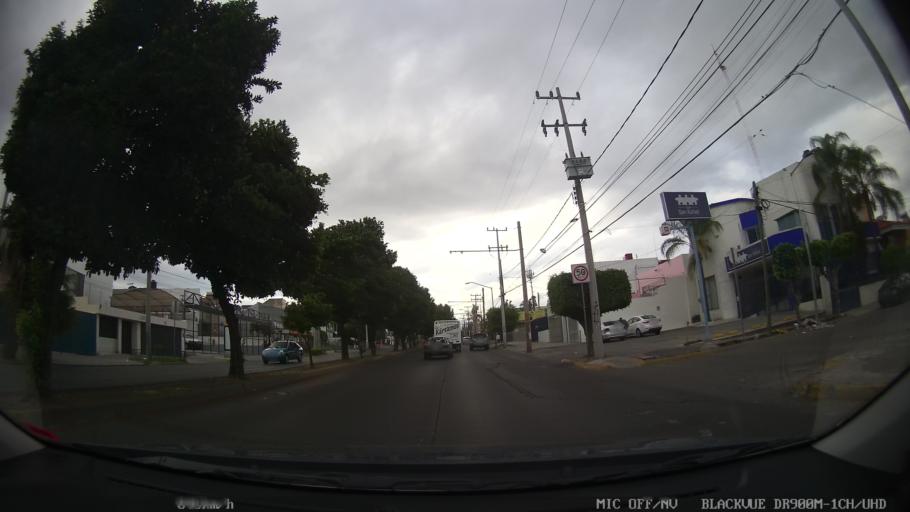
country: MX
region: Jalisco
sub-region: Zapopan
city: Zapopan
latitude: 20.6963
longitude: -103.3285
